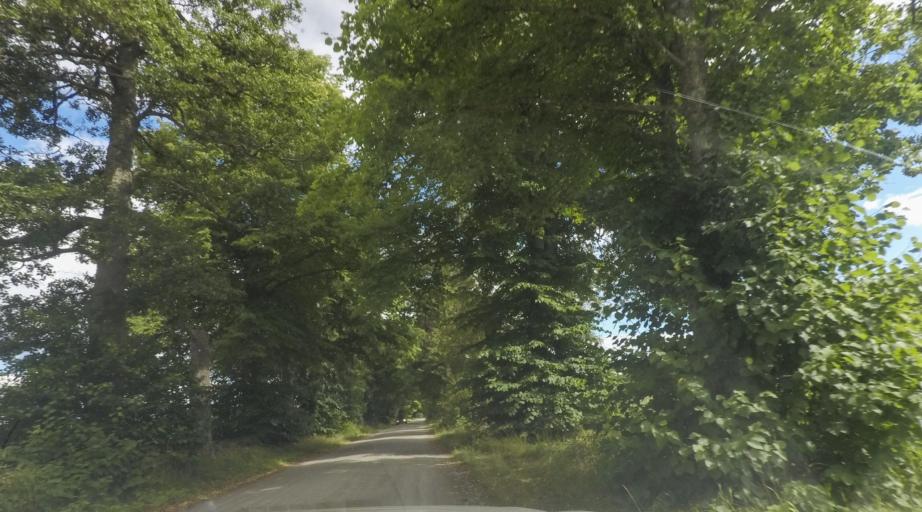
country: SE
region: Stockholm
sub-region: Sodertalje Kommun
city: Pershagen
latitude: 59.1076
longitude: 17.6719
